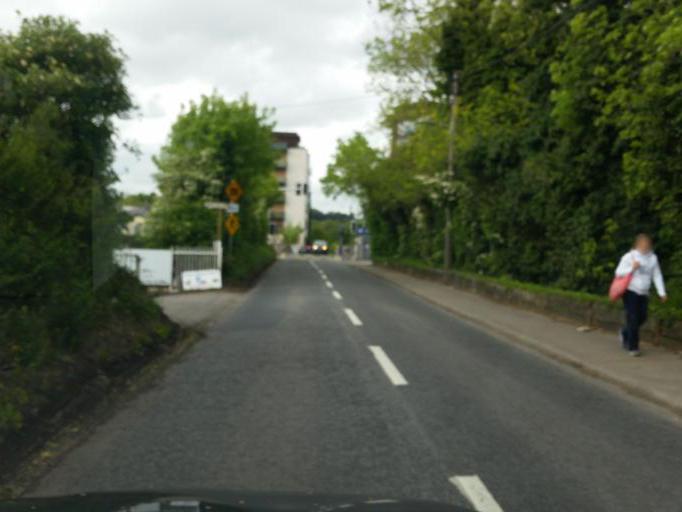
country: IE
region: Leinster
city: Chapelizod
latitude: 53.3746
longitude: -6.3325
